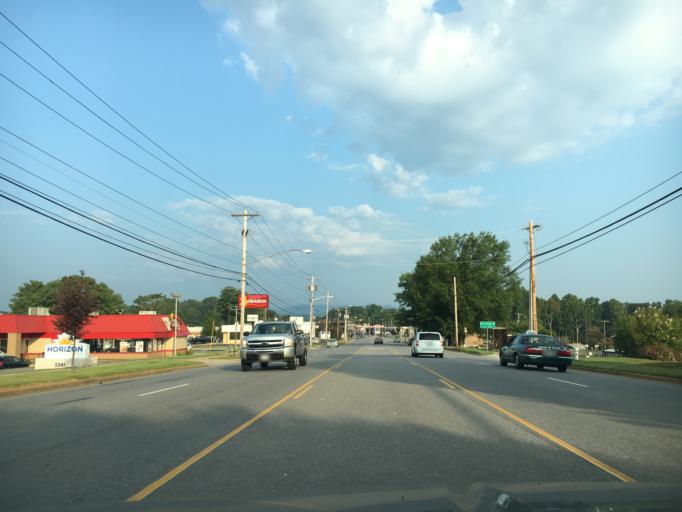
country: US
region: Virginia
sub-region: City of Lynchburg
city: West Lynchburg
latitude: 37.4124
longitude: -79.1724
